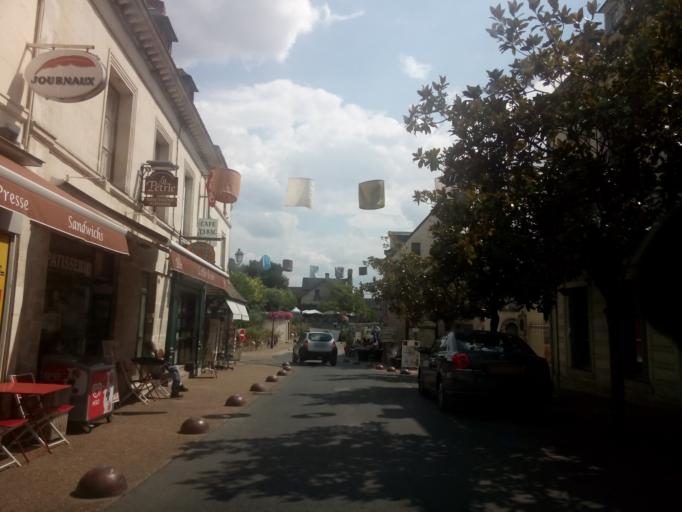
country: FR
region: Centre
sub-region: Departement d'Indre-et-Loire
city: Azay-le-Rideau
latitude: 47.2617
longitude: 0.4661
